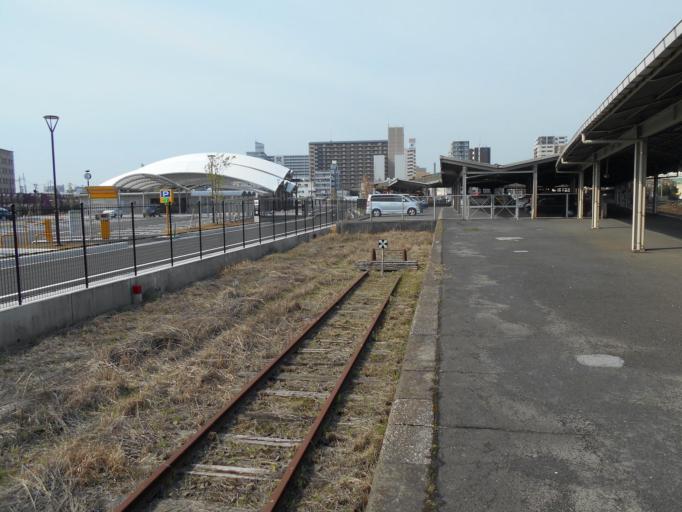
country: JP
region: Kagoshima
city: Kagoshima-shi
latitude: 31.6018
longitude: 130.5638
